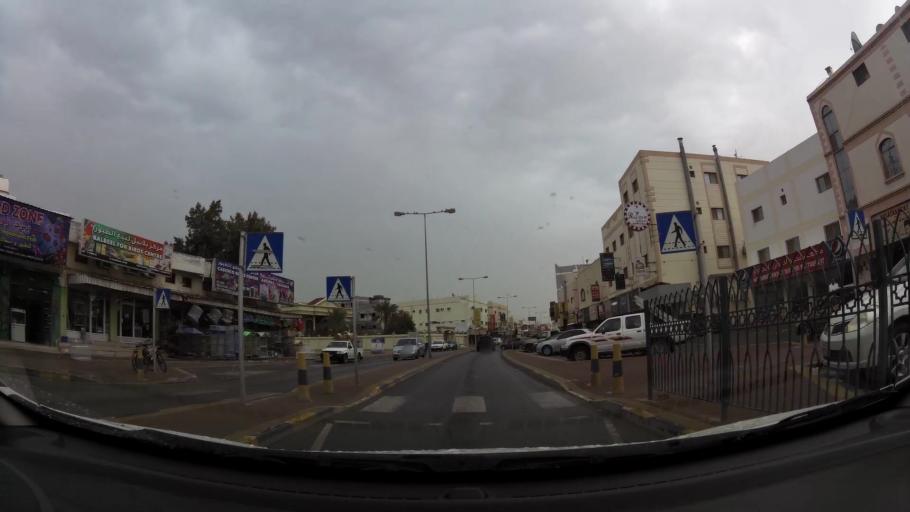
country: BH
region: Northern
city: Madinat `Isa
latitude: 26.1694
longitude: 50.5659
